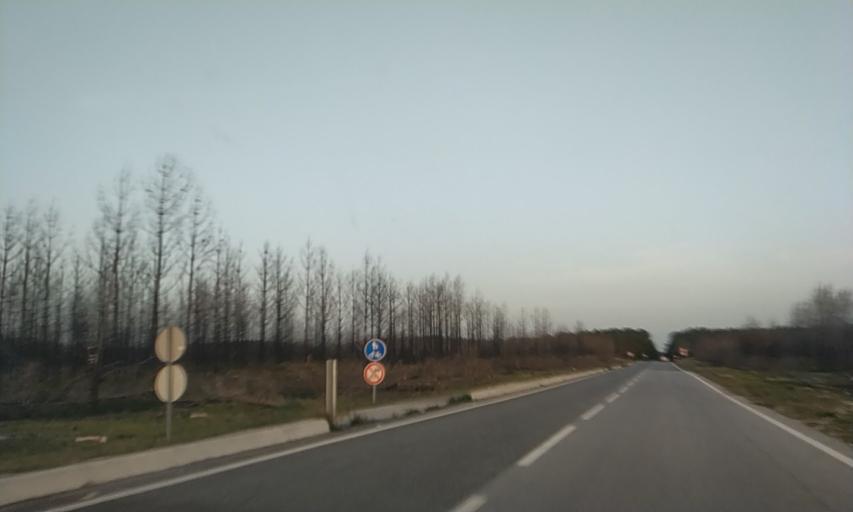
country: PT
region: Leiria
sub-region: Marinha Grande
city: Marinha Grande
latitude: 39.7473
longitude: -8.9635
